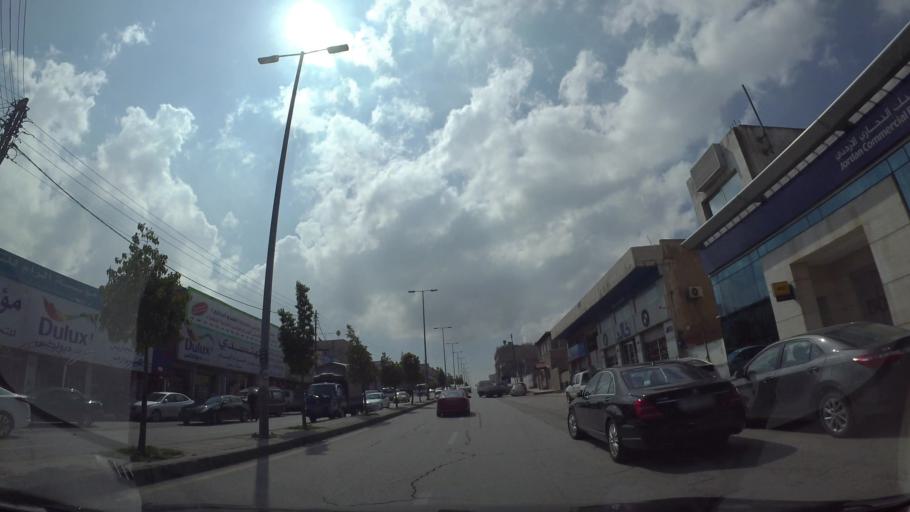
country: JO
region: Zarqa
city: Russeifa
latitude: 31.9856
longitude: 35.9977
